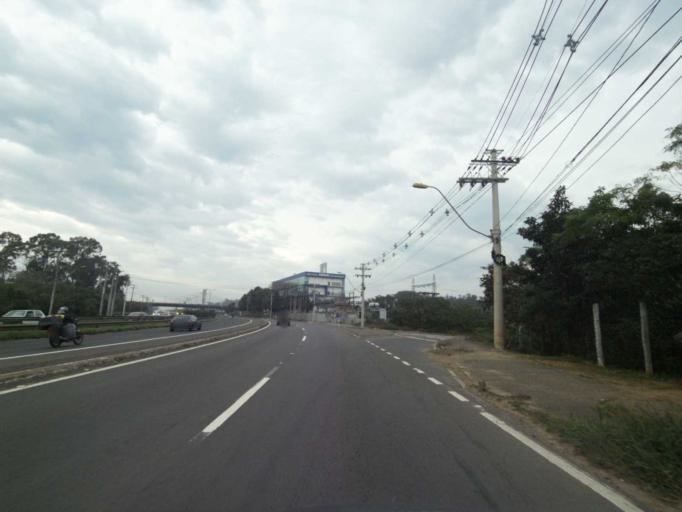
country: BR
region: Rio Grande do Sul
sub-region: Sao Leopoldo
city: Sao Leopoldo
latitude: -29.7846
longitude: -51.1627
